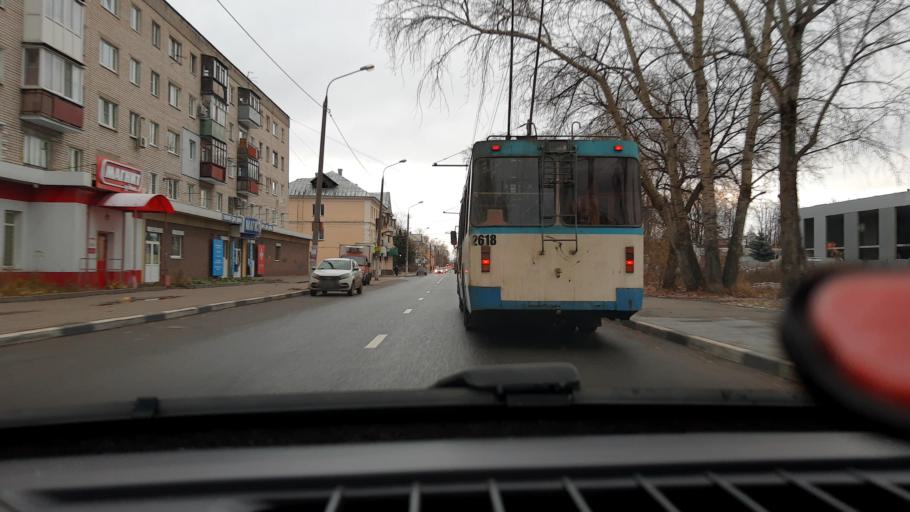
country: RU
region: Nizjnij Novgorod
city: Gorbatovka
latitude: 56.2862
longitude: 43.8503
